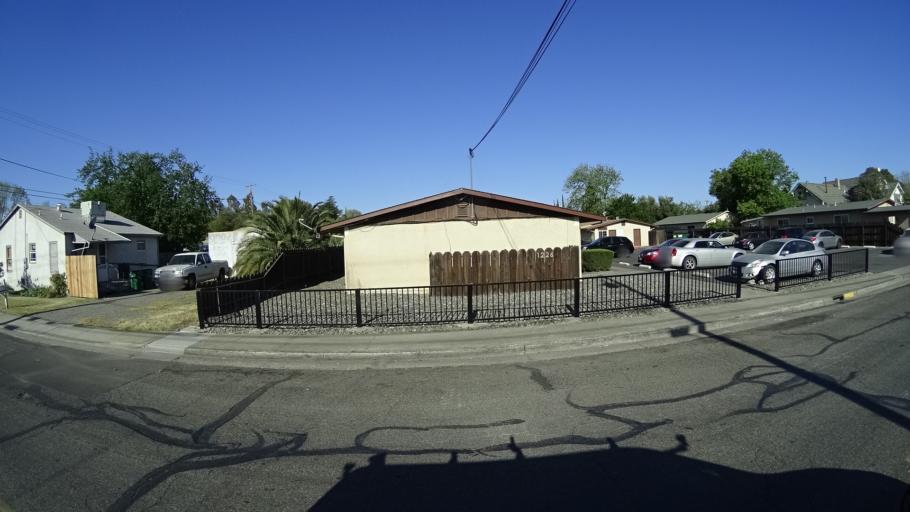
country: US
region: California
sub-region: Glenn County
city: Orland
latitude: 39.7404
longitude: -122.1874
